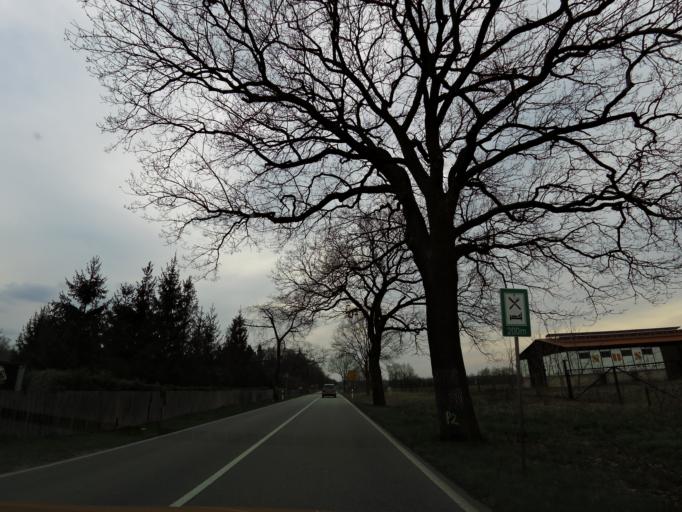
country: DE
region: Brandenburg
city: Beeskow
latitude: 52.1962
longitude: 14.2985
